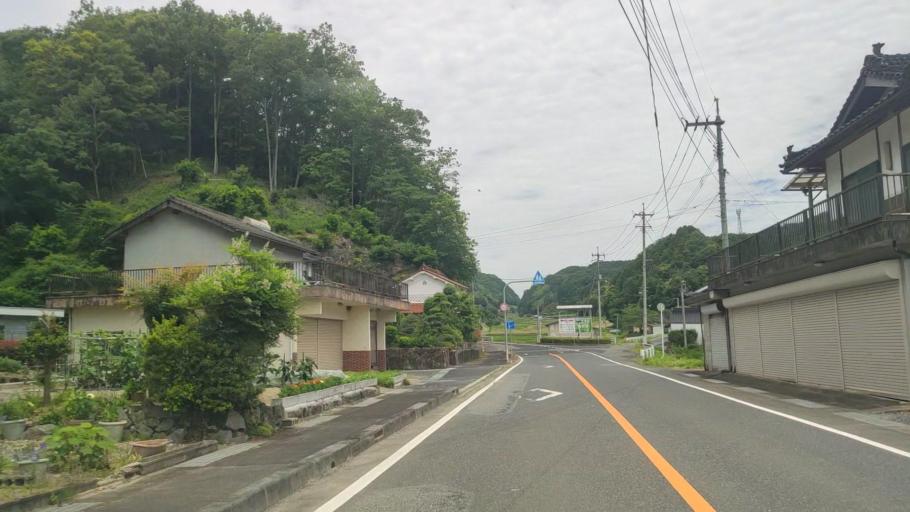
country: JP
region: Okayama
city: Tsuyama
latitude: 35.0848
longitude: 134.2516
